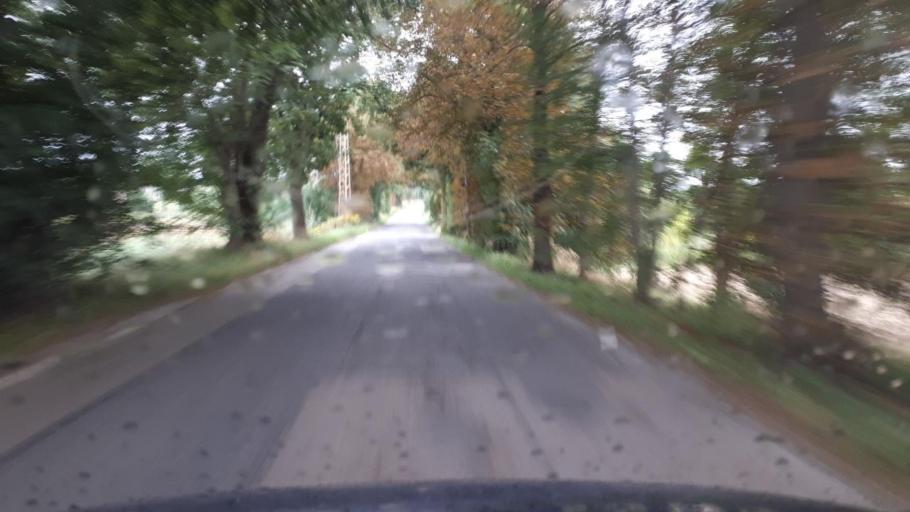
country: PL
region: Silesian Voivodeship
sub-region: Powiat tarnogorski
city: Wieszowa
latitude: 50.3706
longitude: 18.7178
